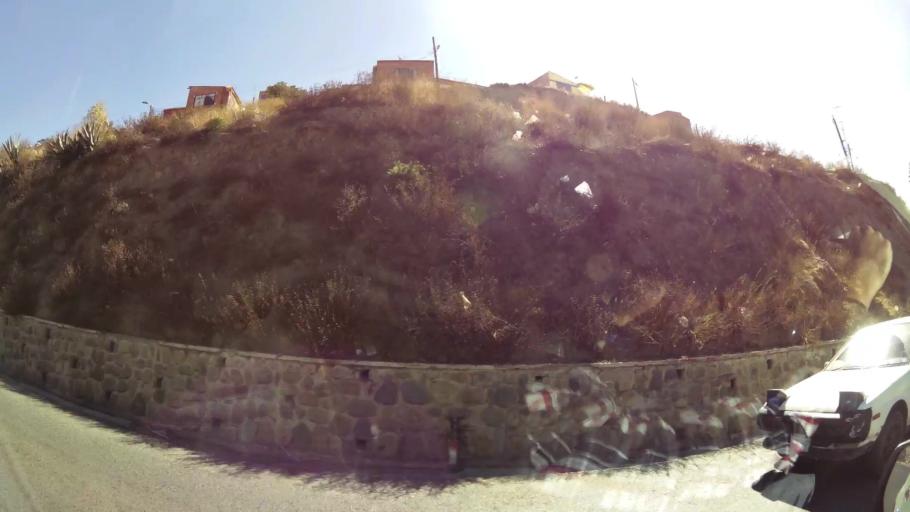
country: BO
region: La Paz
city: La Paz
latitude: -16.4906
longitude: -68.1470
